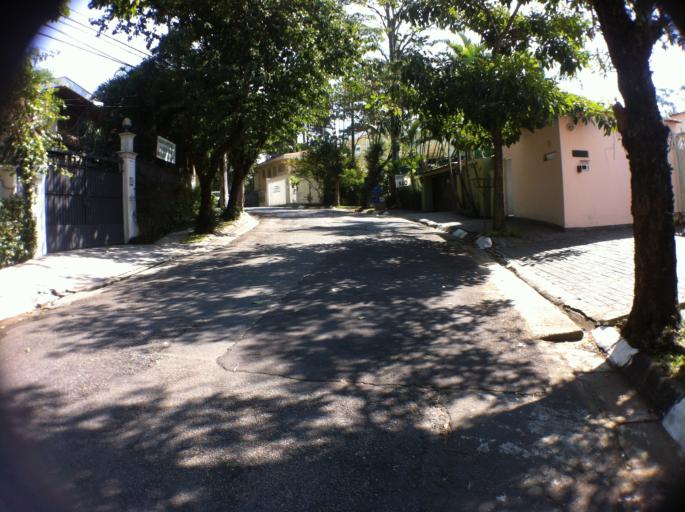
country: BR
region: Sao Paulo
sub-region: Diadema
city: Diadema
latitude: -23.6548
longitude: -46.6838
